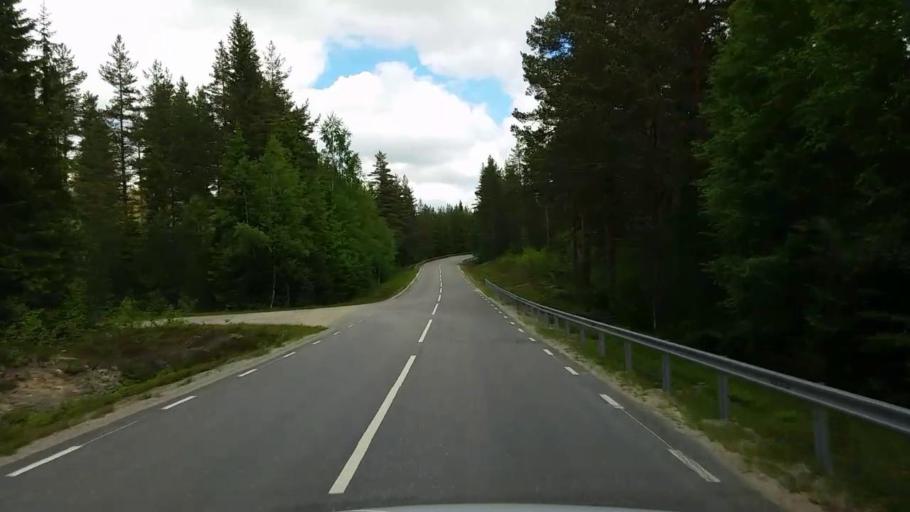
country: SE
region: Gaevleborg
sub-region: Bollnas Kommun
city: Vittsjo
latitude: 61.1167
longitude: 16.1482
